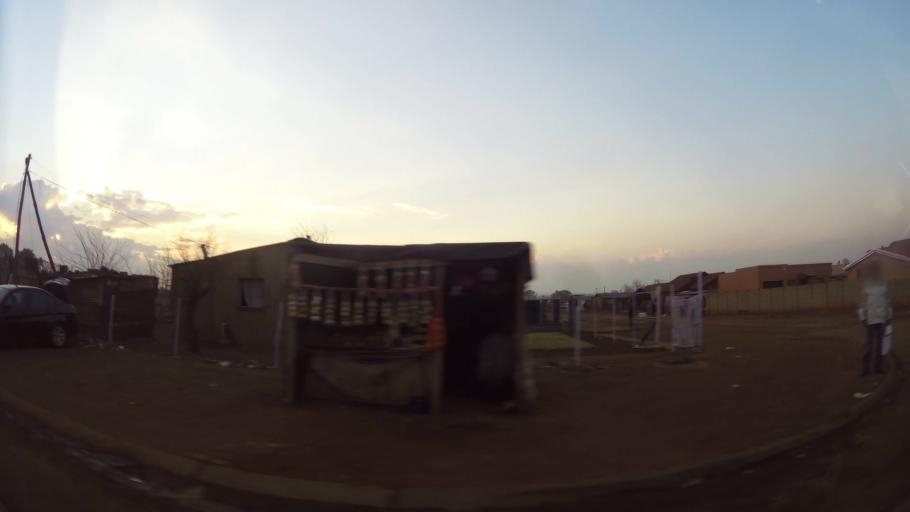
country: ZA
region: Gauteng
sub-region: City of Johannesburg Metropolitan Municipality
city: Orange Farm
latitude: -26.5540
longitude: 27.8664
